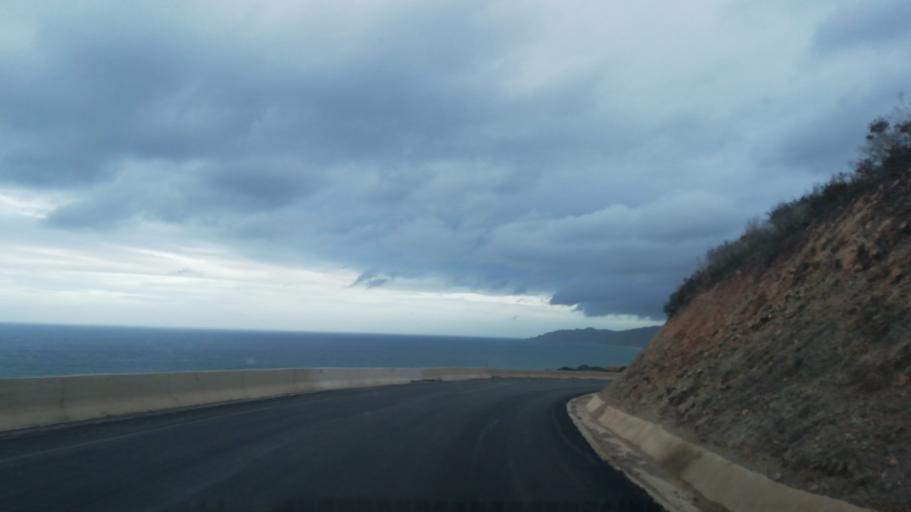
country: DZ
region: Oran
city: Bir el Djir
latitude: 35.7728
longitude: -0.5157
